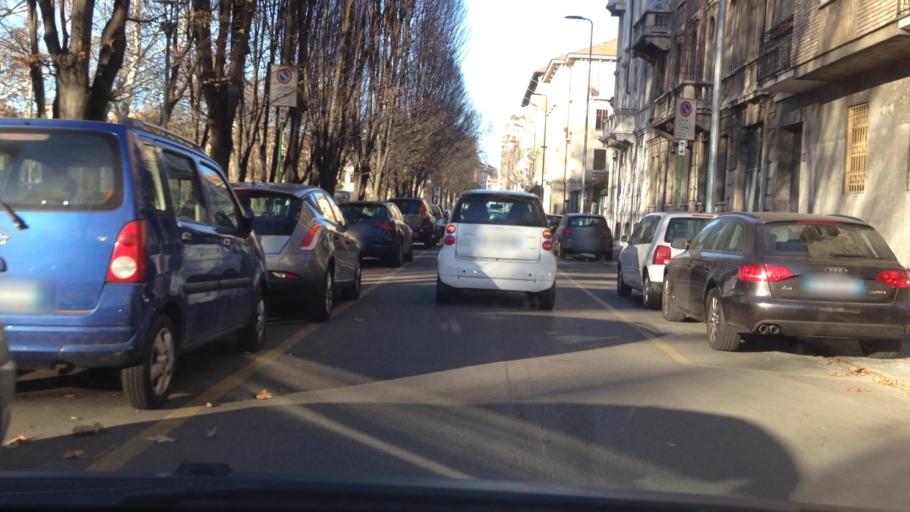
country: IT
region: Lombardy
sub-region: Citta metropolitana di Milano
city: Milano
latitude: 45.4468
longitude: 9.1946
